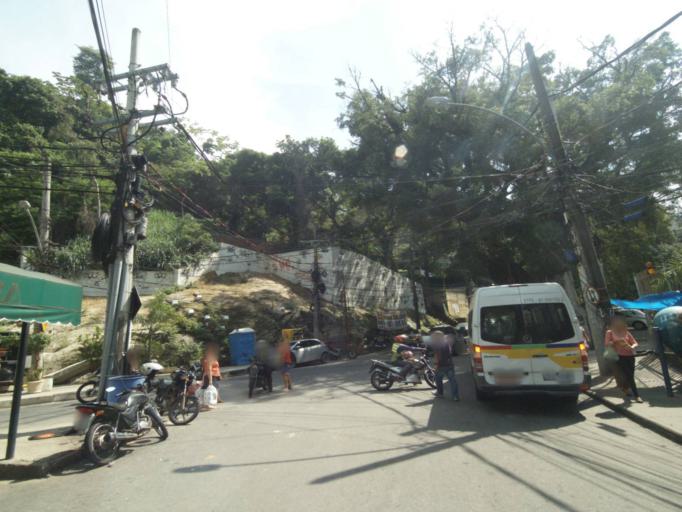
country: BR
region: Rio de Janeiro
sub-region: Rio De Janeiro
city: Rio de Janeiro
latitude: -22.9921
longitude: -43.2537
